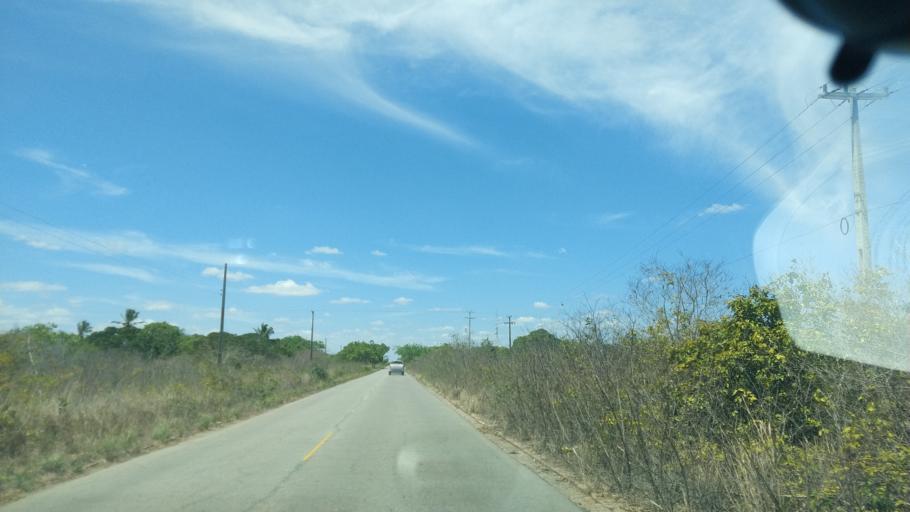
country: BR
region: Rio Grande do Norte
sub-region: Sao Paulo Do Potengi
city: Sao Paulo do Potengi
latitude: -5.9301
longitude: -35.5687
